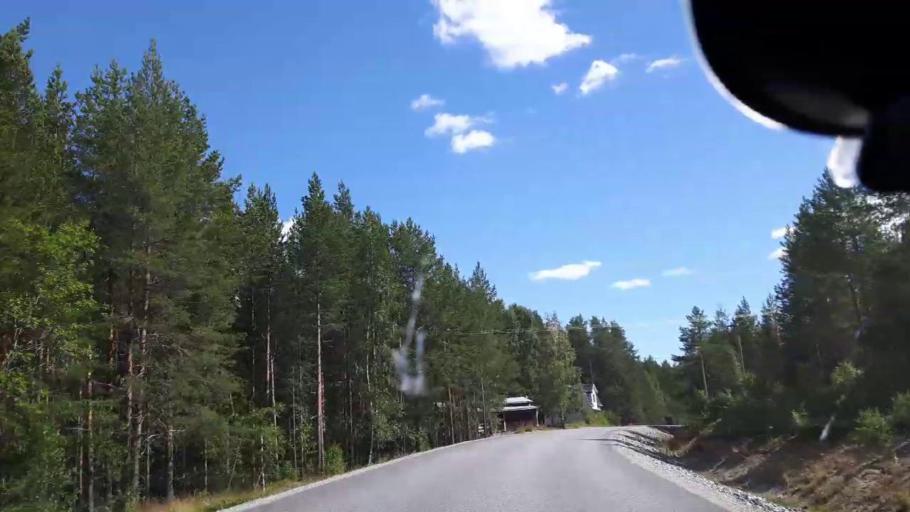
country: SE
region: Vaesternorrland
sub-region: Ange Kommun
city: Fransta
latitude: 62.7003
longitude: 16.3883
